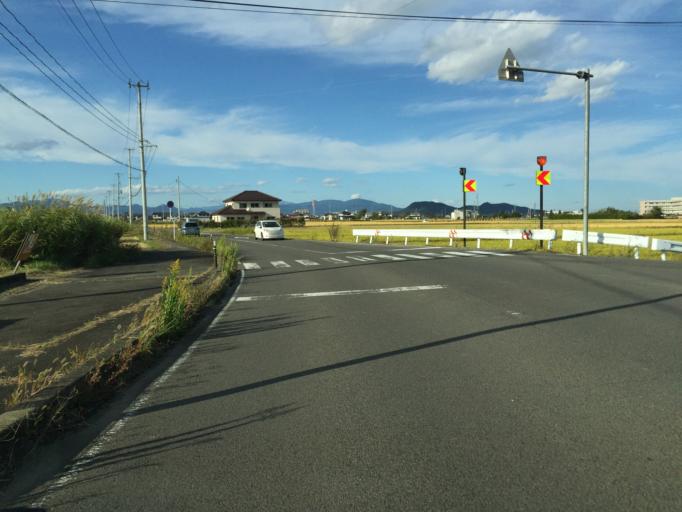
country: JP
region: Fukushima
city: Fukushima-shi
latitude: 37.7164
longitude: 140.4380
